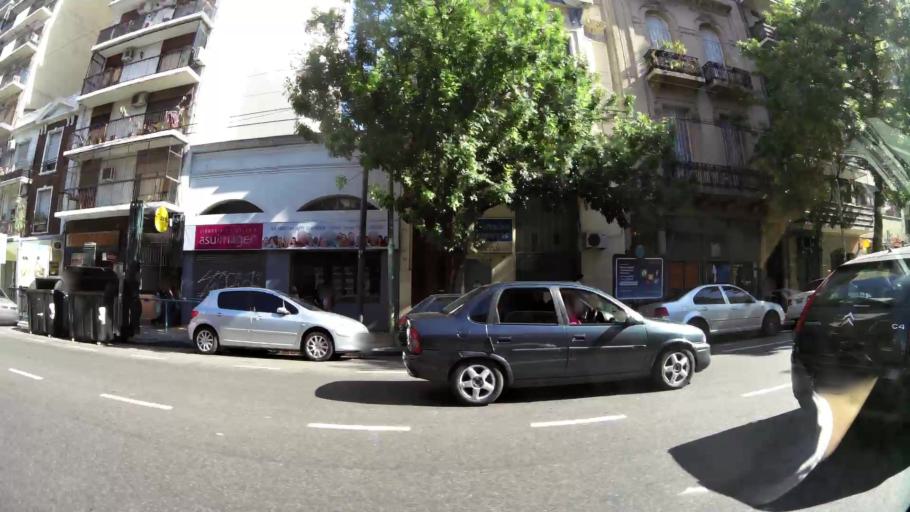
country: AR
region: Buenos Aires F.D.
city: Buenos Aires
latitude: -34.6112
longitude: -58.4153
